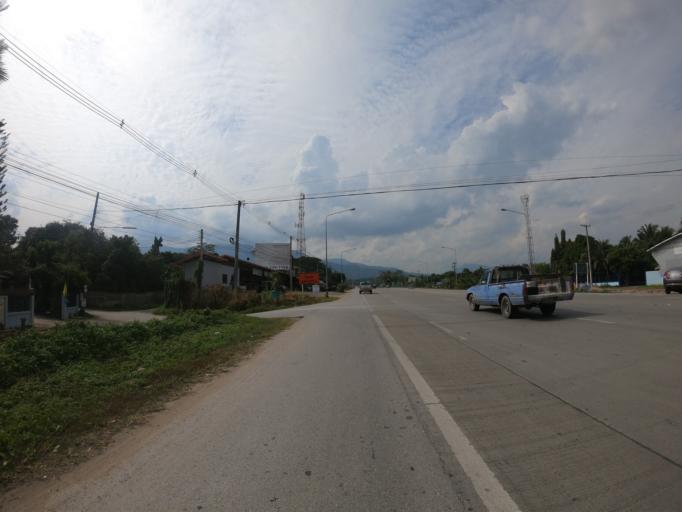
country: TH
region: Chiang Mai
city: San Sai
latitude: 18.8667
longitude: 98.9696
